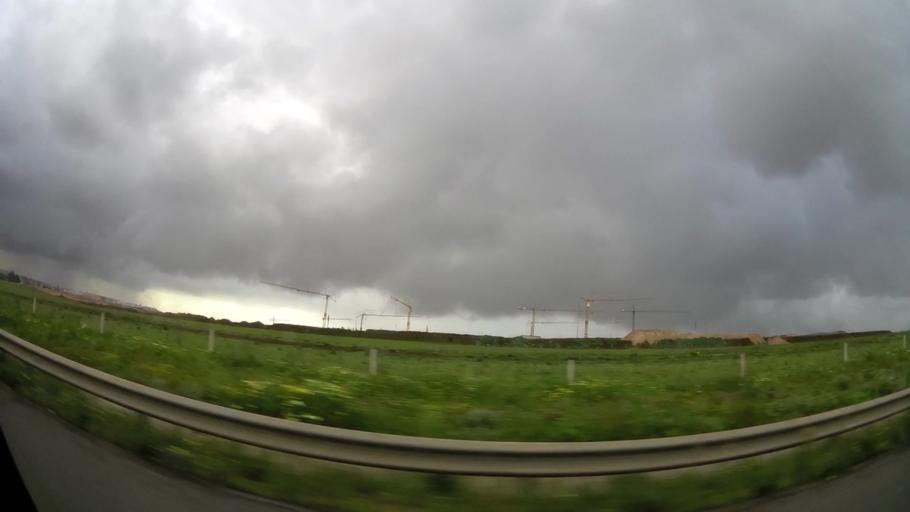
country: MA
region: Grand Casablanca
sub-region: Mediouna
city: Tit Mellil
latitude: 33.5662
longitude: -7.4775
